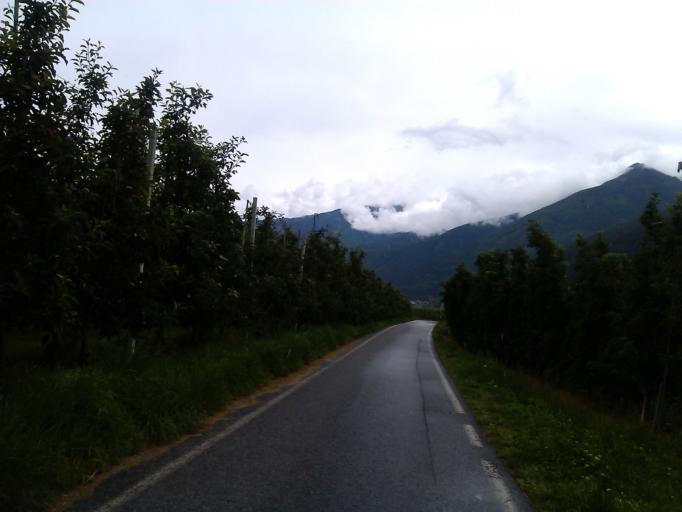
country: IT
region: Trentino-Alto Adige
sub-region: Bolzano
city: Silandro
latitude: 46.6214
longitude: 10.7763
